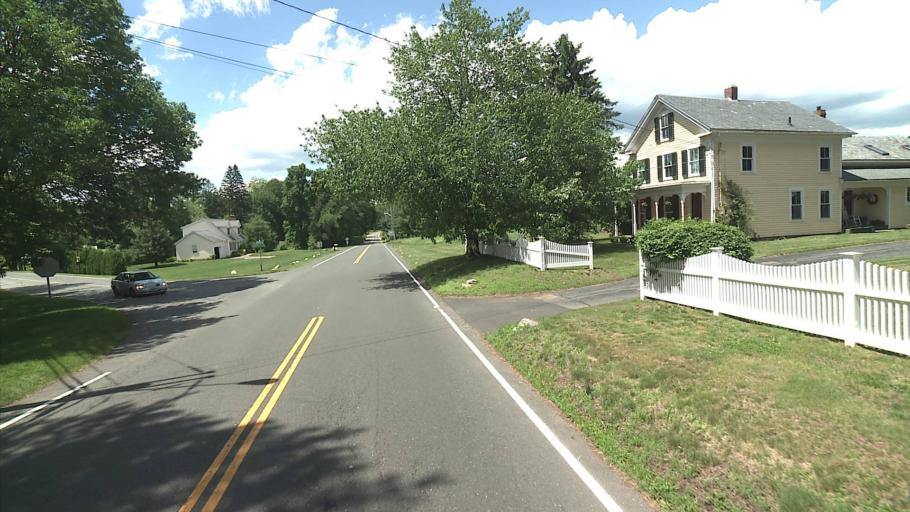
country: US
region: Massachusetts
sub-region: Hampden County
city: East Longmeadow
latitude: 42.0334
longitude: -72.4914
